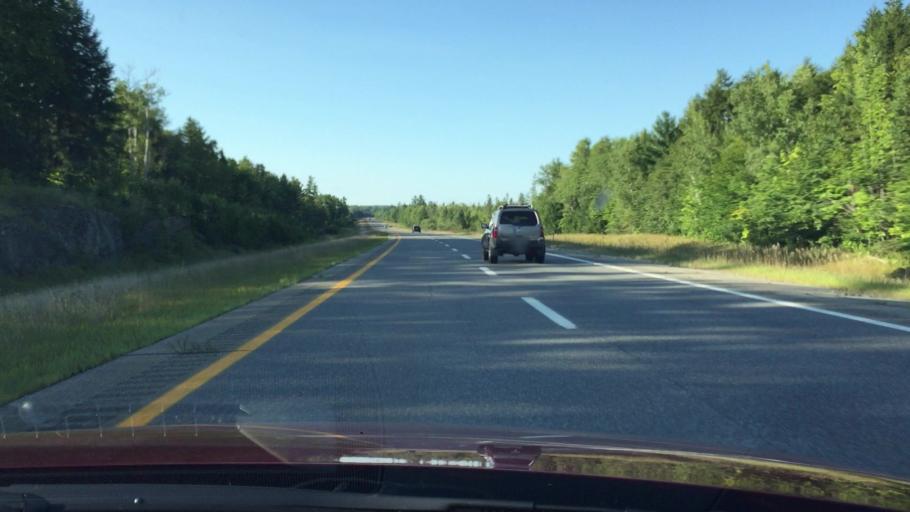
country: US
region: Maine
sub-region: Penobscot County
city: Lincoln
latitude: 45.4304
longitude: -68.5884
